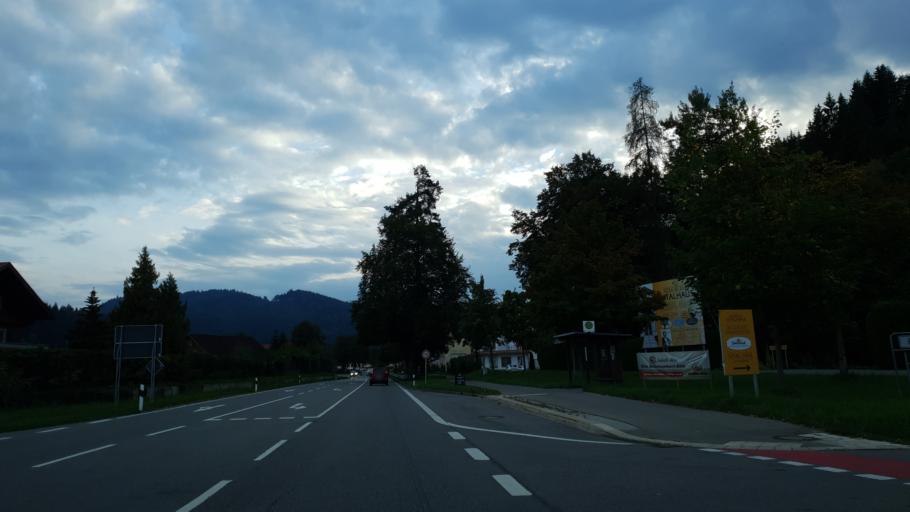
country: DE
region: Bavaria
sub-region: Swabia
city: Weitnau
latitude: 47.6609
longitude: 10.0927
